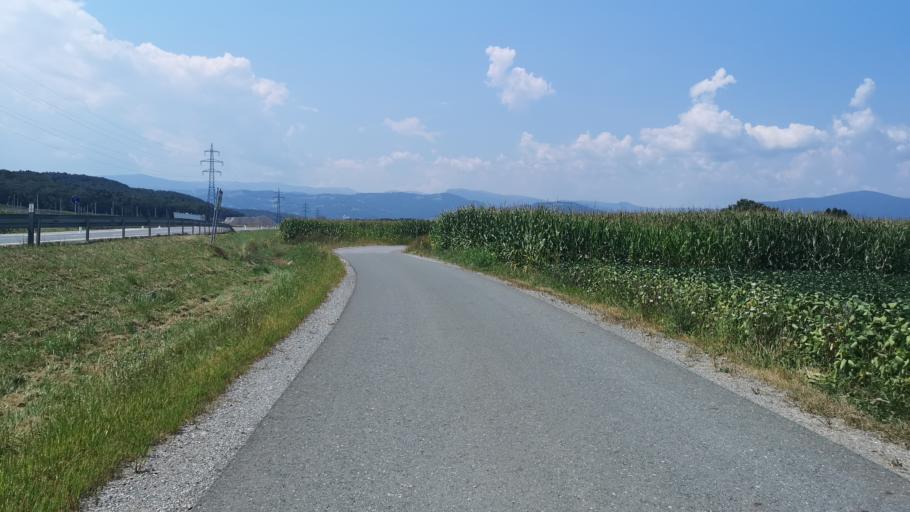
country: AT
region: Styria
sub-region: Politischer Bezirk Deutschlandsberg
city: Gross Sankt Florian
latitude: 46.8154
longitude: 15.3038
